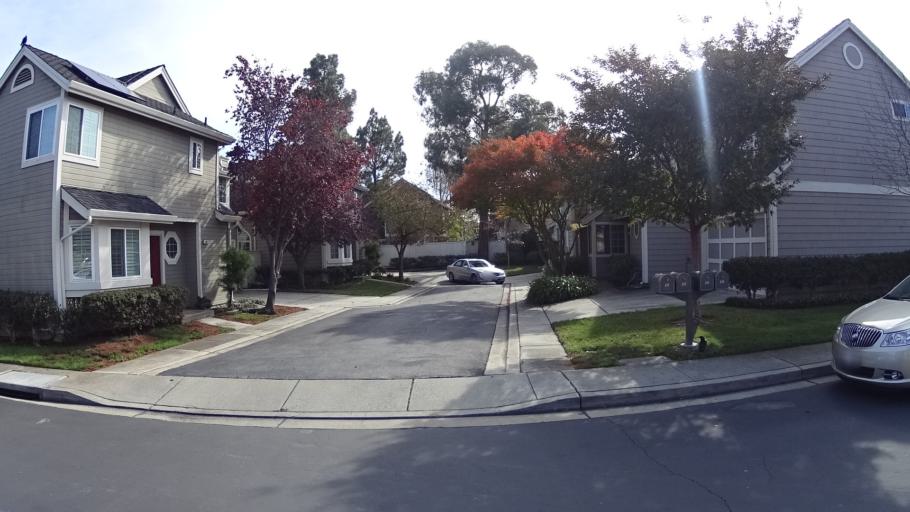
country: US
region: California
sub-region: San Mateo County
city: Belmont
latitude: 37.5356
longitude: -122.2681
